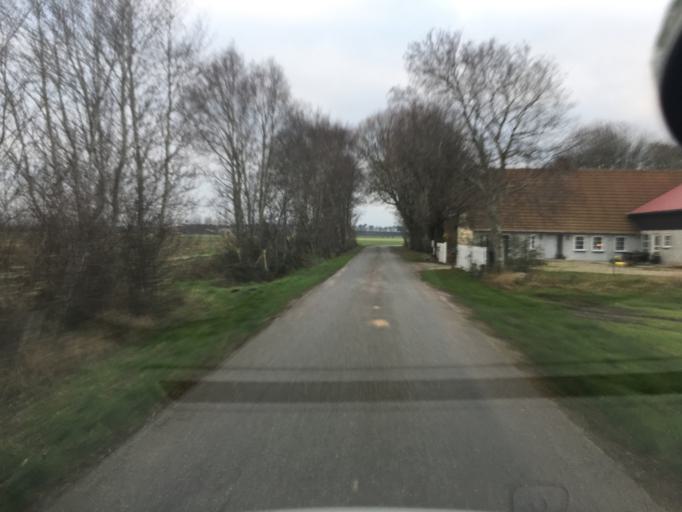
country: DK
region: South Denmark
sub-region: Tonder Kommune
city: Logumkloster
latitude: 55.0604
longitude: 9.0664
